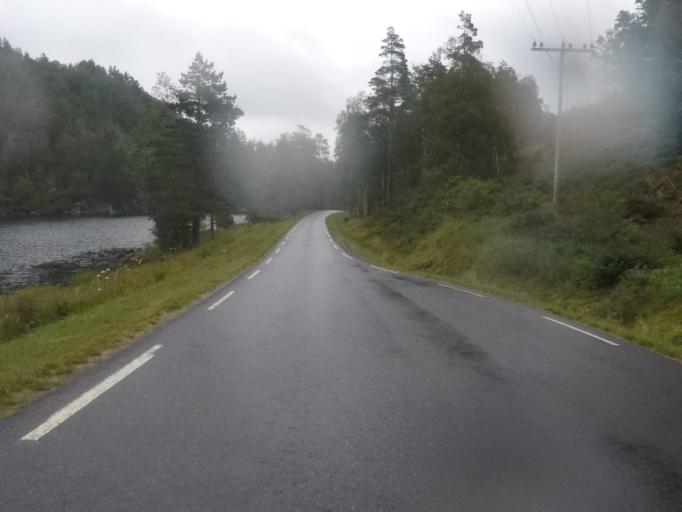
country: NO
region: Vest-Agder
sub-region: Lyngdal
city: Lyngdal
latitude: 58.2489
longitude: 7.0796
